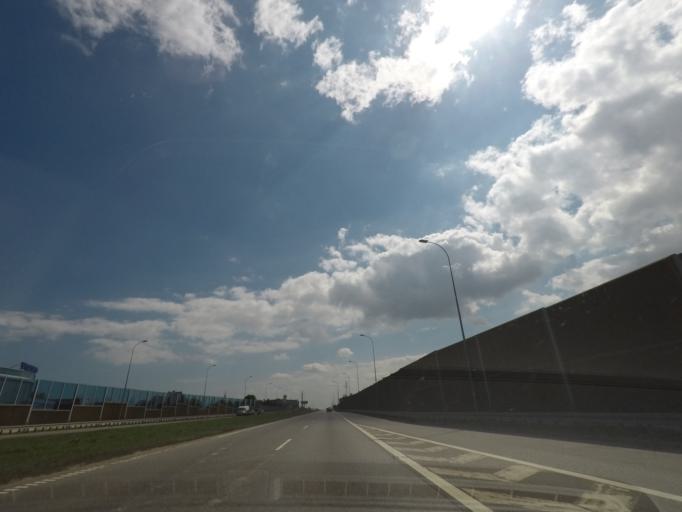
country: PL
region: Pomeranian Voivodeship
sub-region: Powiat gdanski
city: Kowale
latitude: 54.3428
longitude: 18.5469
